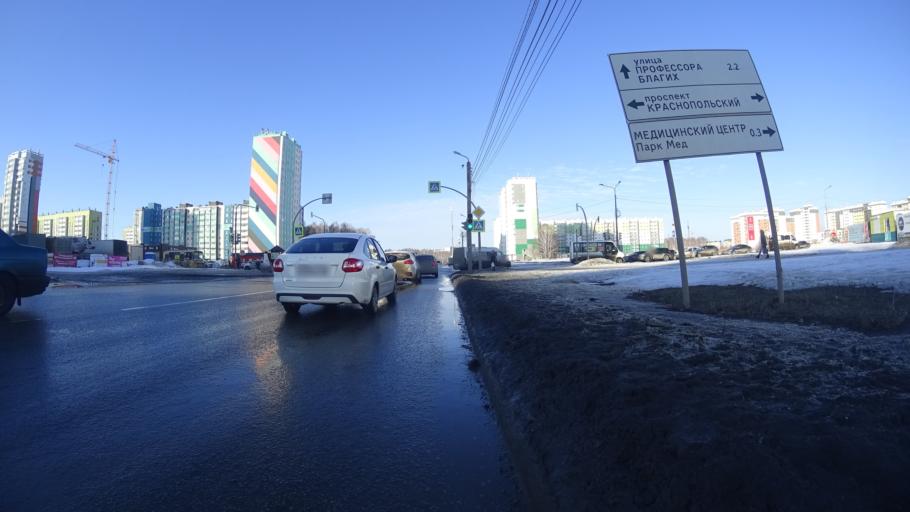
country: RU
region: Chelyabinsk
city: Roshchino
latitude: 55.2096
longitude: 61.2844
